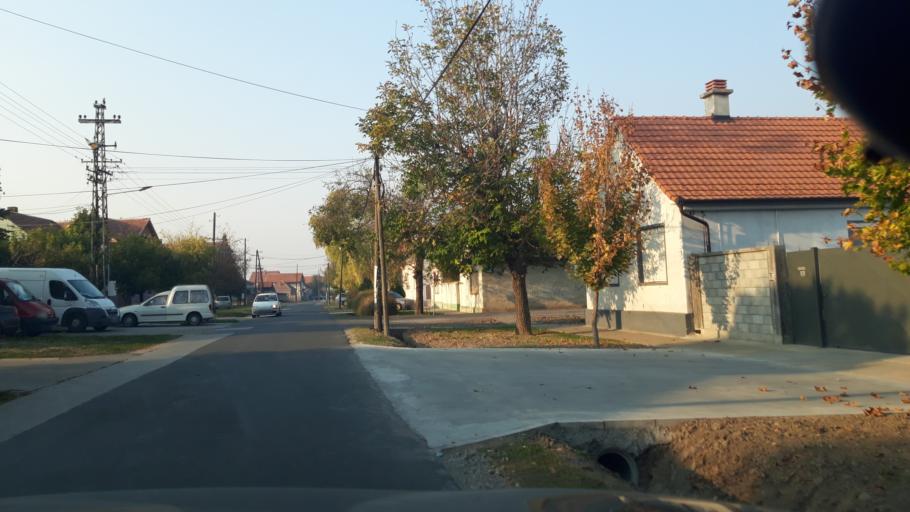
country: RS
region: Autonomna Pokrajina Vojvodina
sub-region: Sremski Okrug
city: Stara Pazova
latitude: 44.9940
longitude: 20.1463
